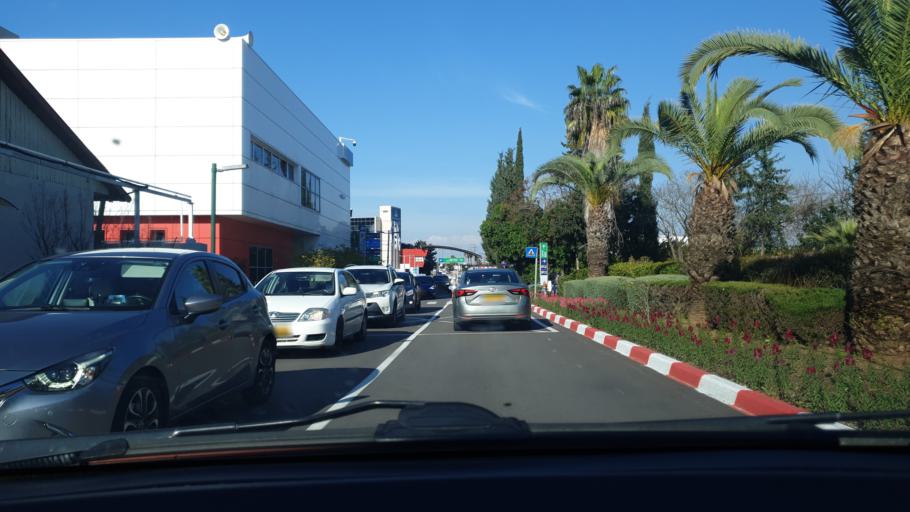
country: IL
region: Central District
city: Kefar Habad
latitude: 31.9665
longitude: 34.8418
